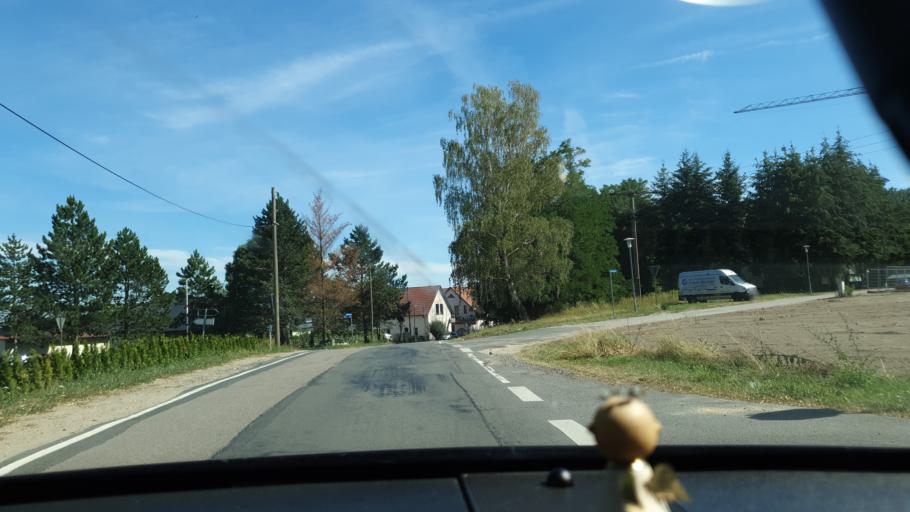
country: DE
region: Saxony
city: Doberschutz
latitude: 51.4847
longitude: 12.7774
